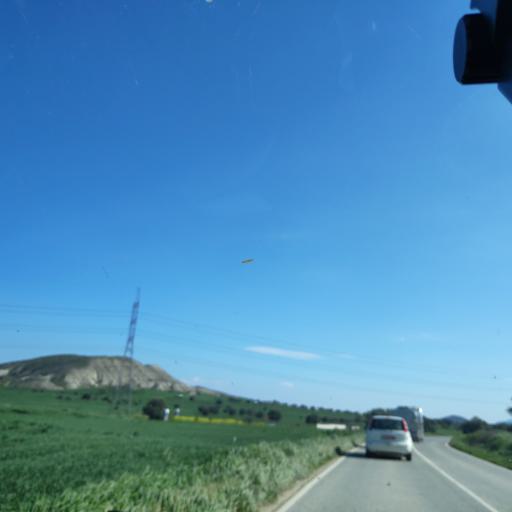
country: CY
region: Lefkosia
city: Tseri
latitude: 35.0201
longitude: 33.3315
